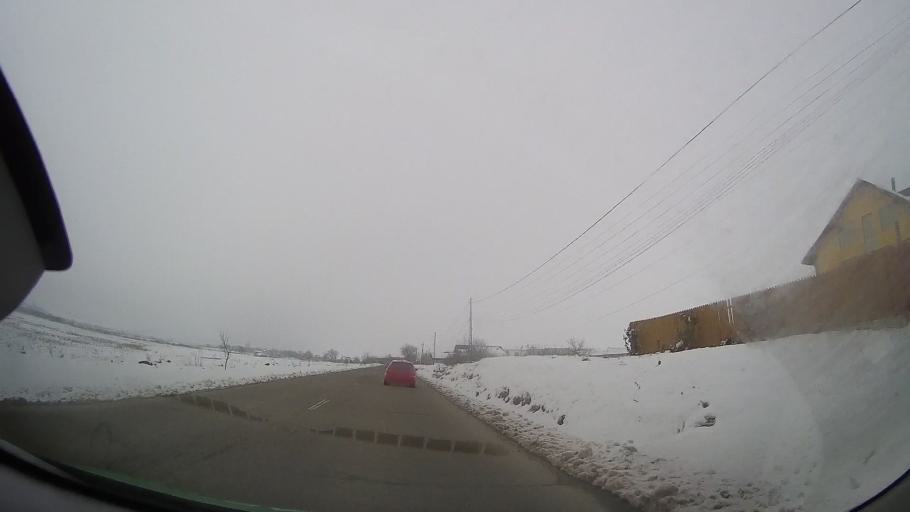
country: RO
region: Vaslui
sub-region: Comuna Negresti
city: Negresti
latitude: 46.8384
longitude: 27.4365
